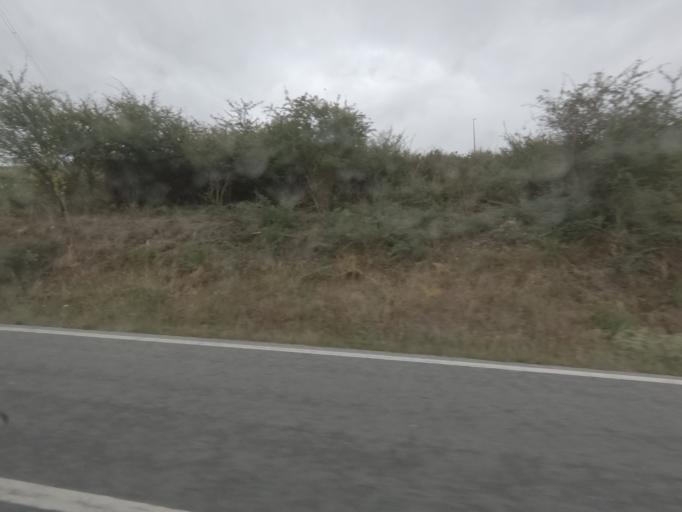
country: PT
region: Vila Real
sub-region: Peso da Regua
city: Peso da Regua
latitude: 41.1360
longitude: -7.7675
